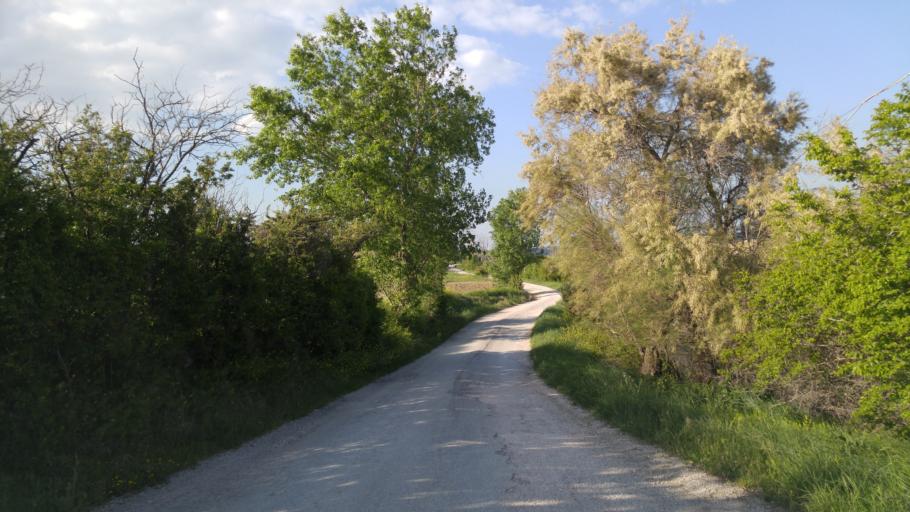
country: IT
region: The Marches
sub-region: Provincia di Pesaro e Urbino
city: Monte Porzio
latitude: 43.7149
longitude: 13.0587
